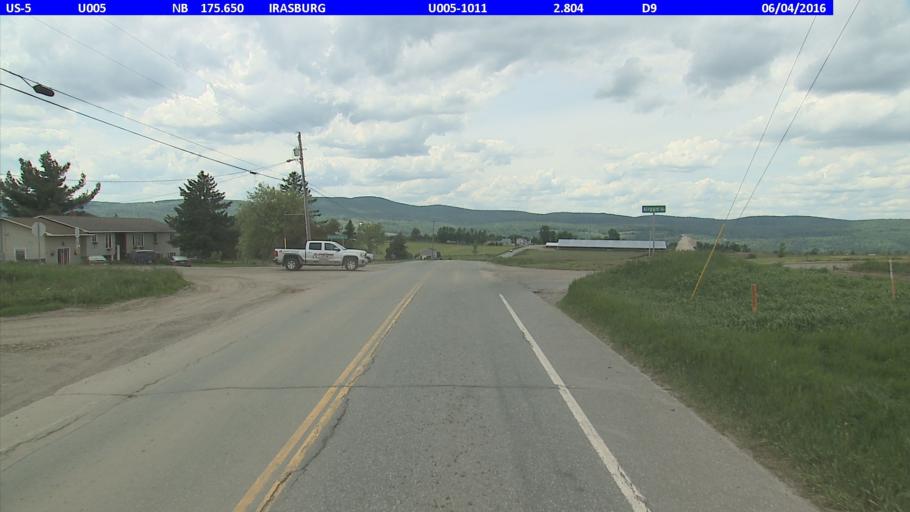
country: US
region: Vermont
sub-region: Orleans County
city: Newport
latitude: 44.8352
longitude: -72.2518
